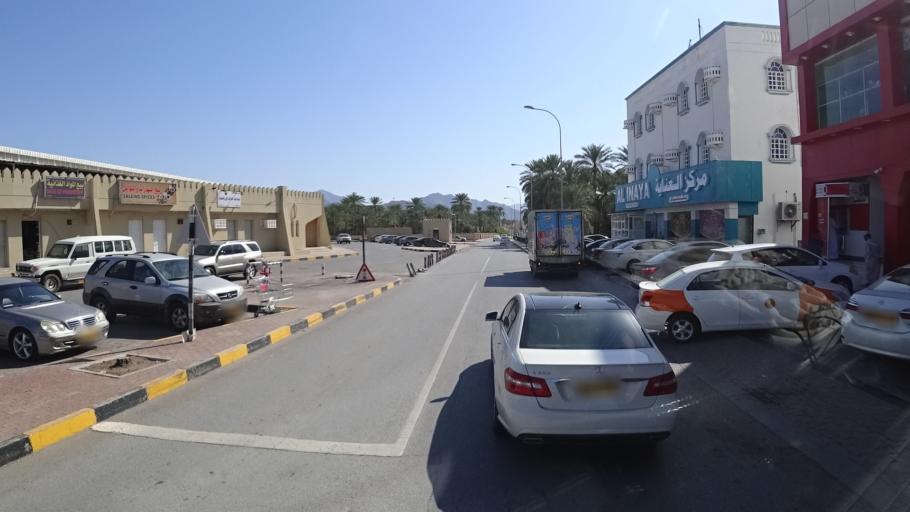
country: OM
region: Al Batinah
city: Rustaq
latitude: 23.3942
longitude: 57.4231
